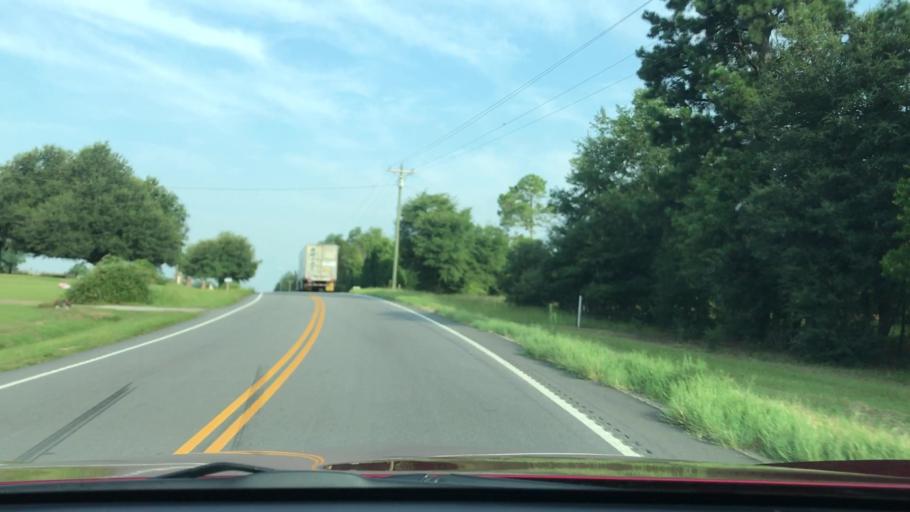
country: US
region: South Carolina
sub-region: Barnwell County
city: Blackville
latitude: 33.5605
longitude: -81.1698
